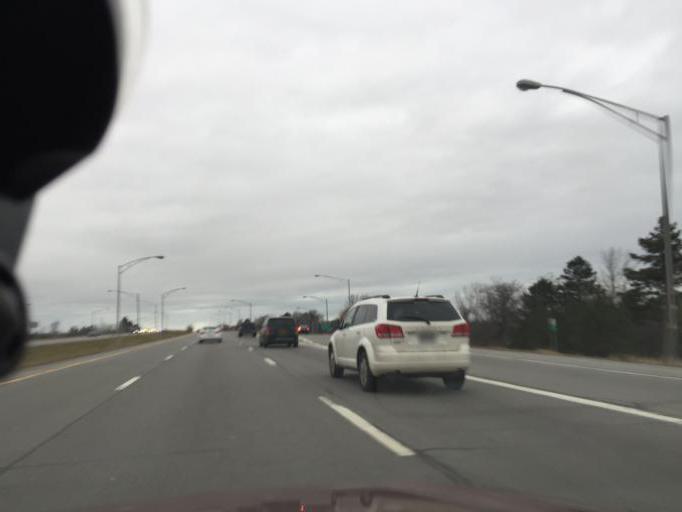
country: US
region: New York
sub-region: Monroe County
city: North Gates
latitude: 43.1760
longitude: -77.6832
